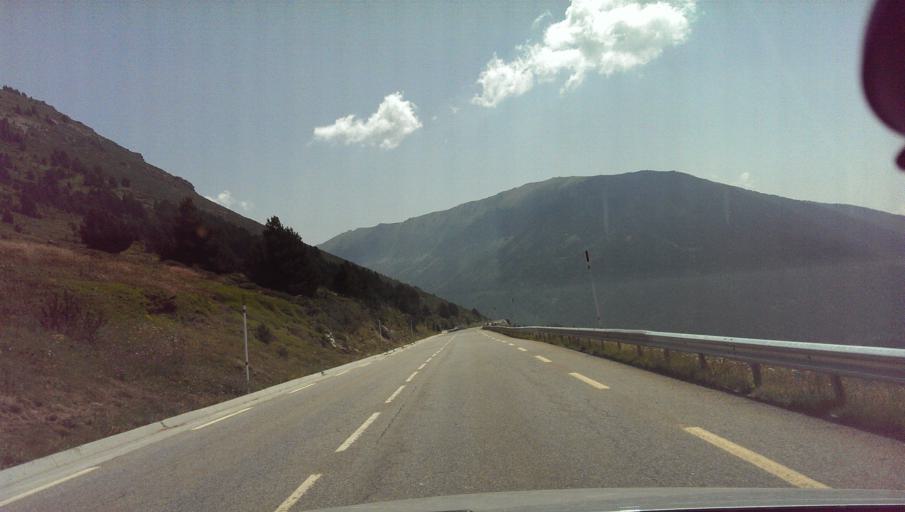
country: AD
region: Encamp
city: Pas de la Casa
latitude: 42.5580
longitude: 1.8161
